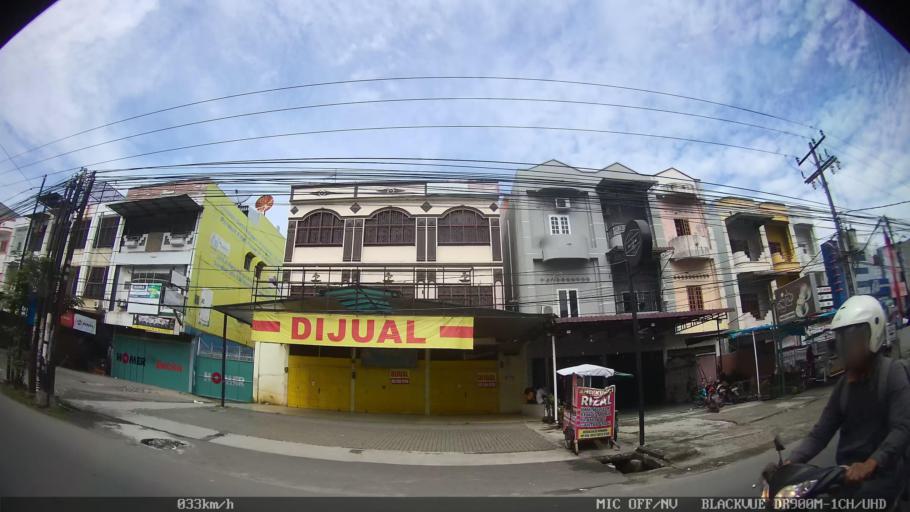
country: ID
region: North Sumatra
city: Medan
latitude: 3.6195
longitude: 98.7072
